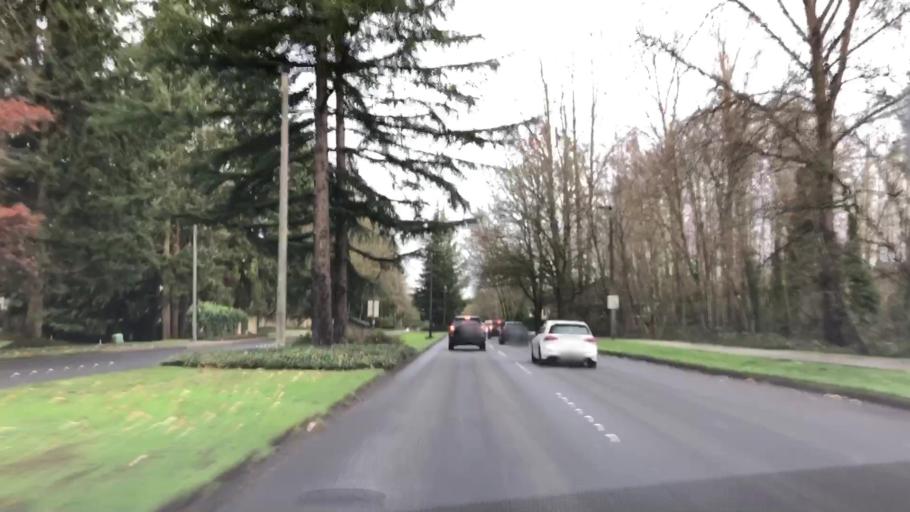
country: US
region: Washington
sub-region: King County
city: Eastgate
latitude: 47.6129
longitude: -122.1430
